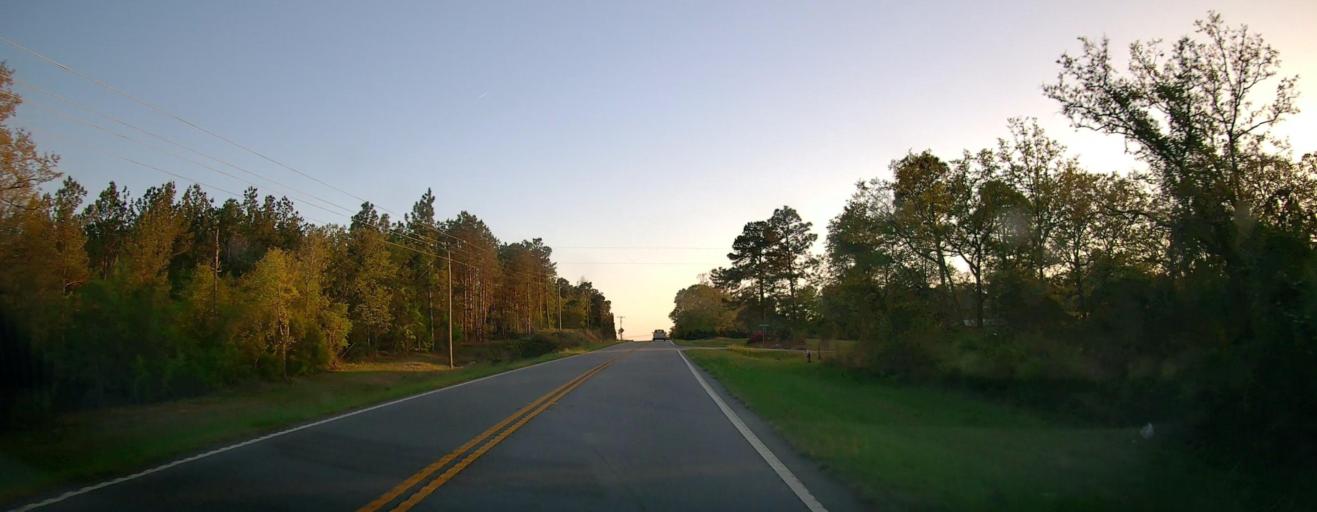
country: US
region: Georgia
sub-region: Talbot County
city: Talbotton
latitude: 32.5059
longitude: -84.6079
